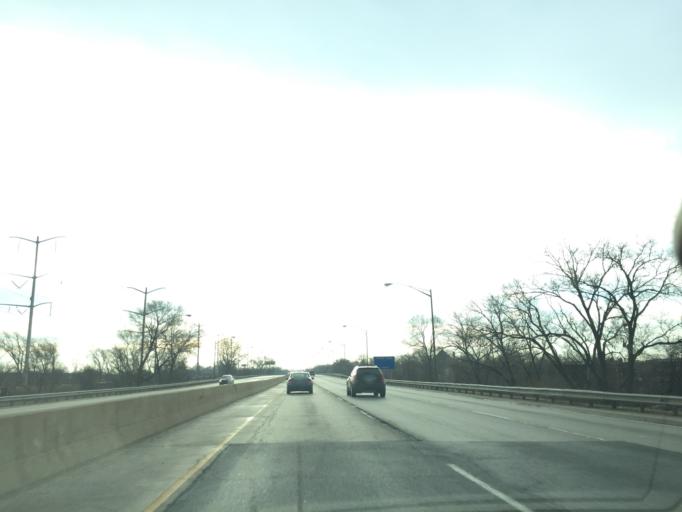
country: US
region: Illinois
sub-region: Cook County
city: Chicago
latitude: 41.7652
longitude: -87.6074
